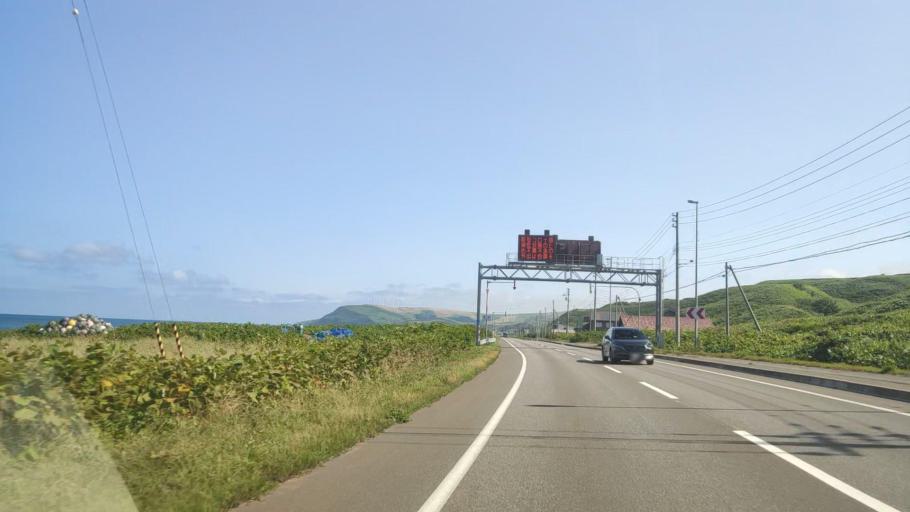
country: JP
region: Hokkaido
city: Makubetsu
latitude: 45.4374
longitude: 141.8624
